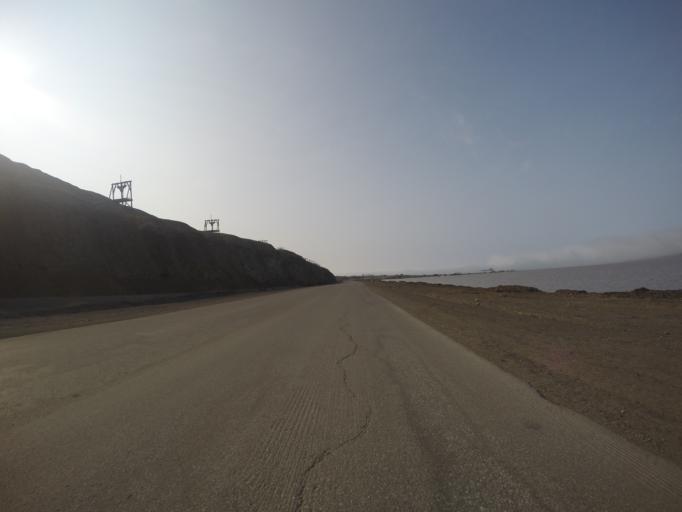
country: SJ
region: Svalbard
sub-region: Spitsbergen
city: Longyearbyen
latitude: 78.2327
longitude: 15.5671
